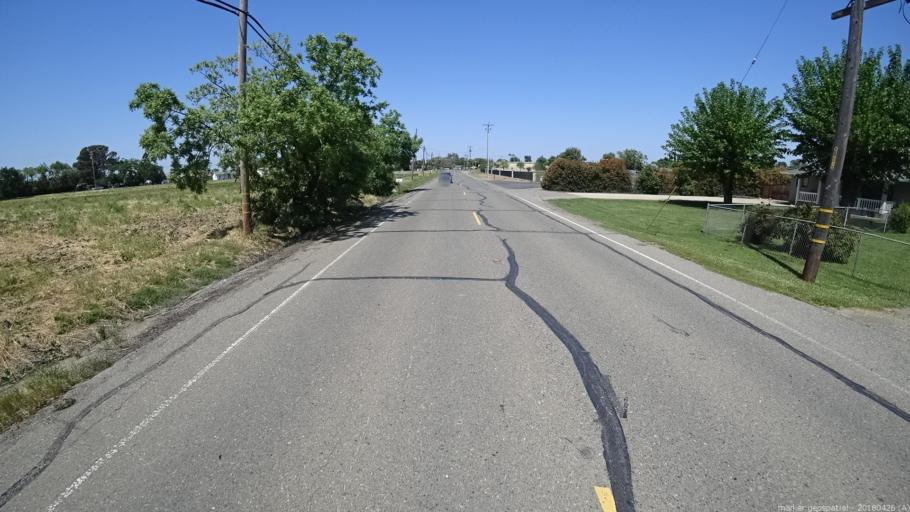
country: US
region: California
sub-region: Yolo County
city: West Sacramento
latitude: 38.5300
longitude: -121.5560
